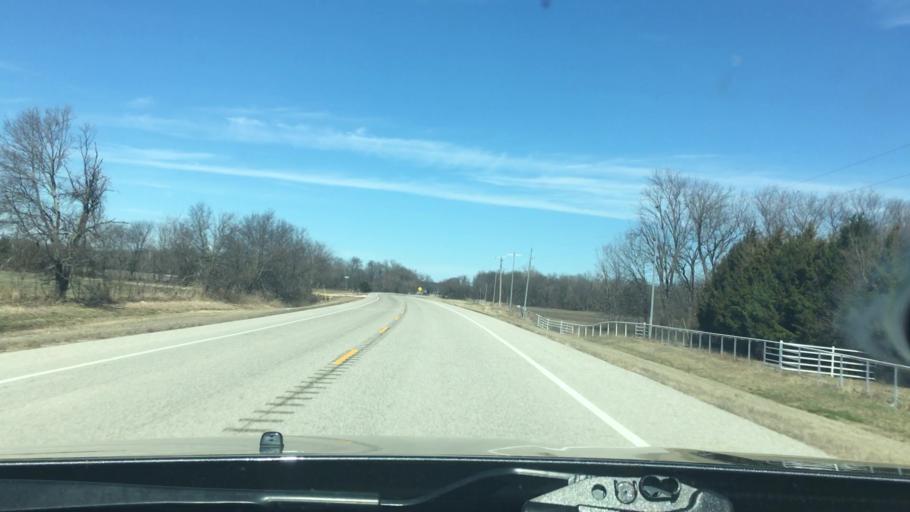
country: US
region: Oklahoma
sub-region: Murray County
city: Sulphur
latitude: 34.3855
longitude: -96.9509
